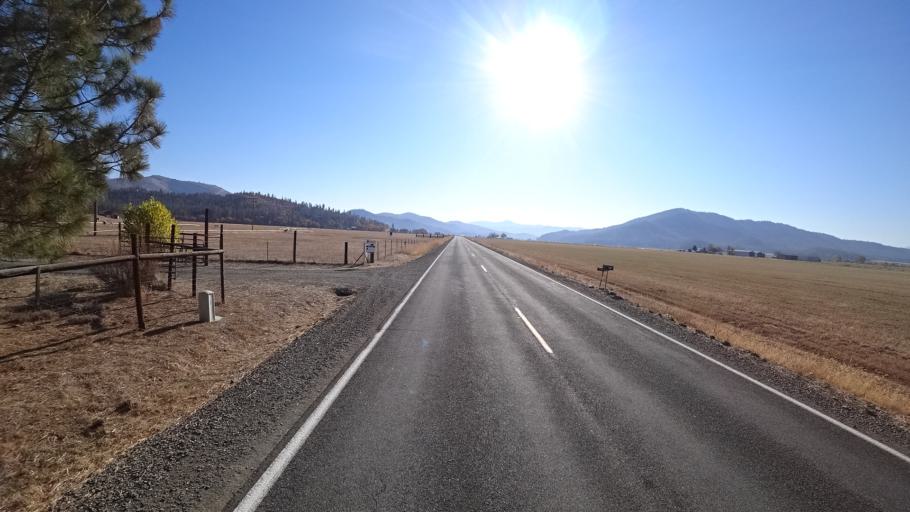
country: US
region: California
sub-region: Siskiyou County
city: Yreka
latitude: 41.6340
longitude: -122.9012
